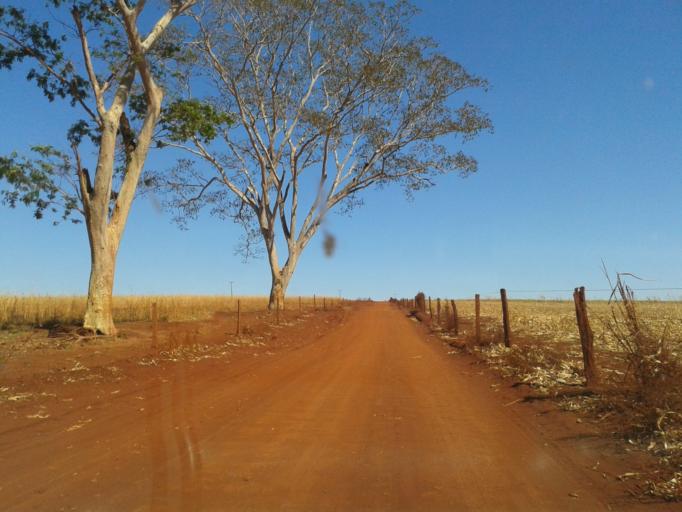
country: BR
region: Minas Gerais
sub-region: Centralina
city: Centralina
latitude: -18.5842
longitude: -49.1312
